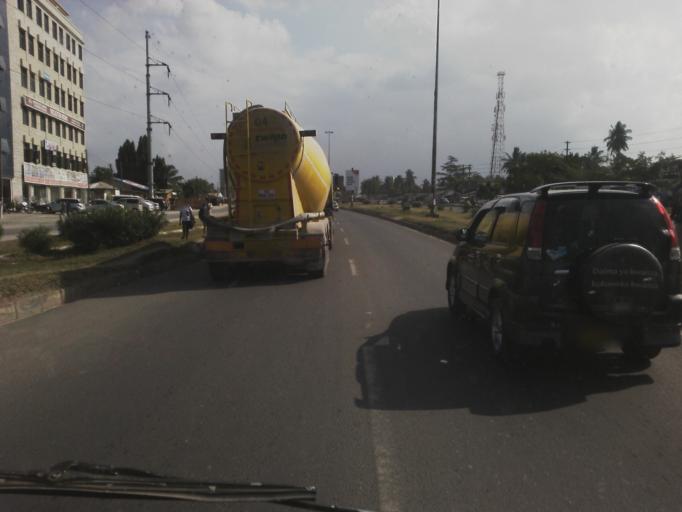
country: TZ
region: Dar es Salaam
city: Magomeni
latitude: -6.7691
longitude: 39.2251
